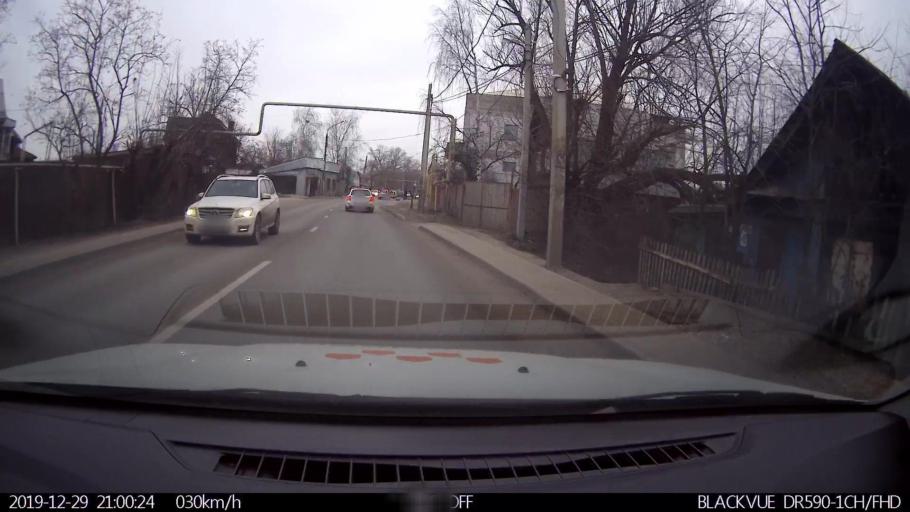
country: RU
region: Nizjnij Novgorod
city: Nizhniy Novgorod
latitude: 56.3046
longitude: 43.9254
